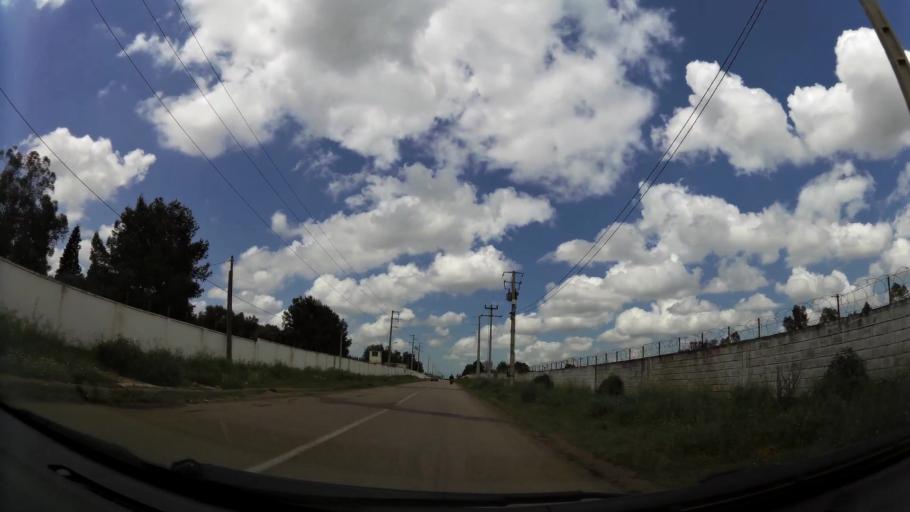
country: MA
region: Chaouia-Ouardigha
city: Nouaseur
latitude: 33.3881
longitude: -7.5763
